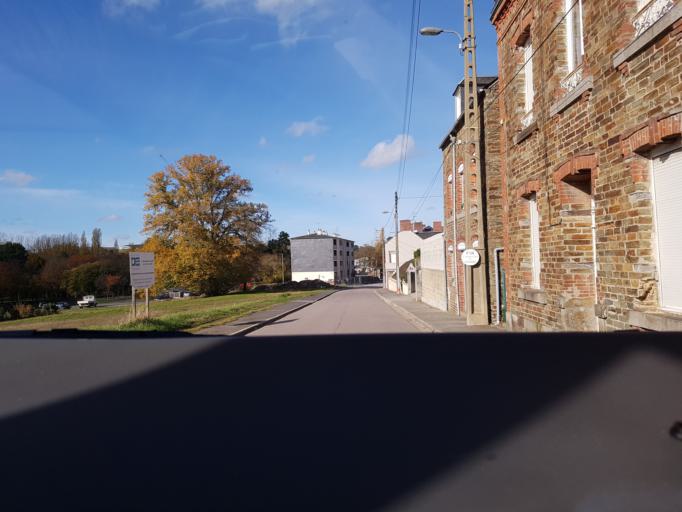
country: FR
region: Lower Normandy
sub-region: Departement du Calvados
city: Conde-sur-Noireau
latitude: 48.8537
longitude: -0.5542
